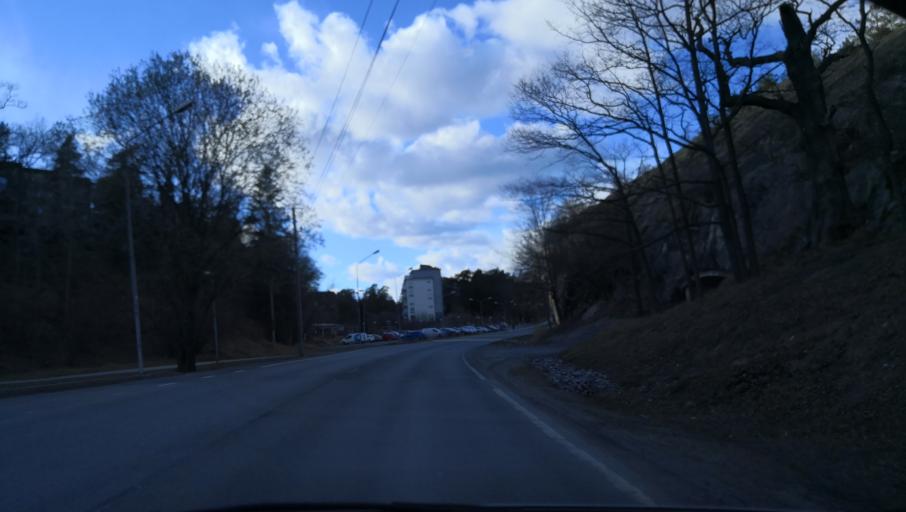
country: SE
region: Stockholm
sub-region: Varmdo Kommun
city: Gustavsberg
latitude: 59.3295
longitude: 18.3920
